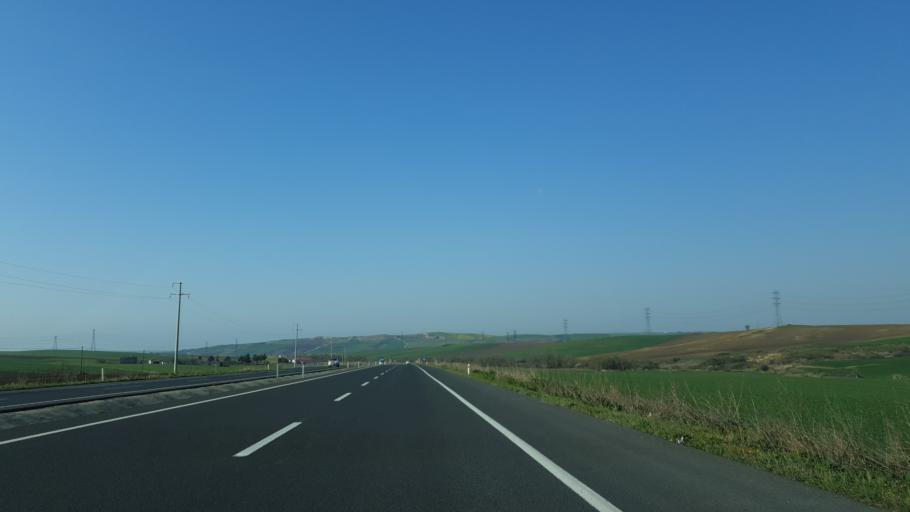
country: TR
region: Tekirdag
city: Corlu
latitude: 41.0903
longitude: 27.7464
